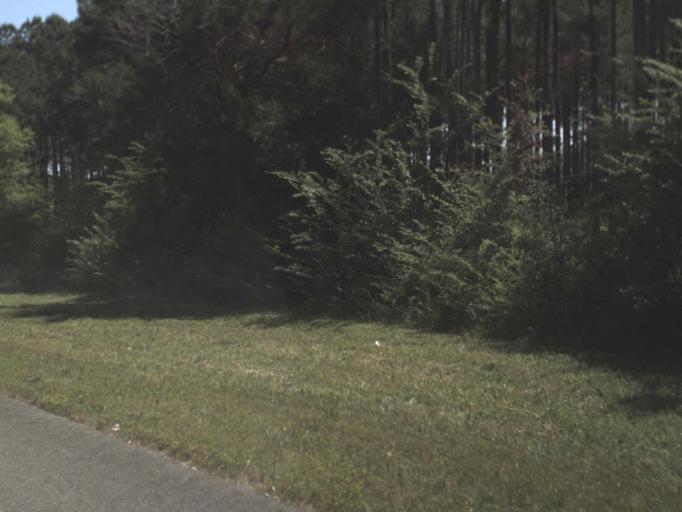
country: US
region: Alabama
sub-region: Escambia County
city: East Brewton
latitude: 30.8982
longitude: -86.9945
